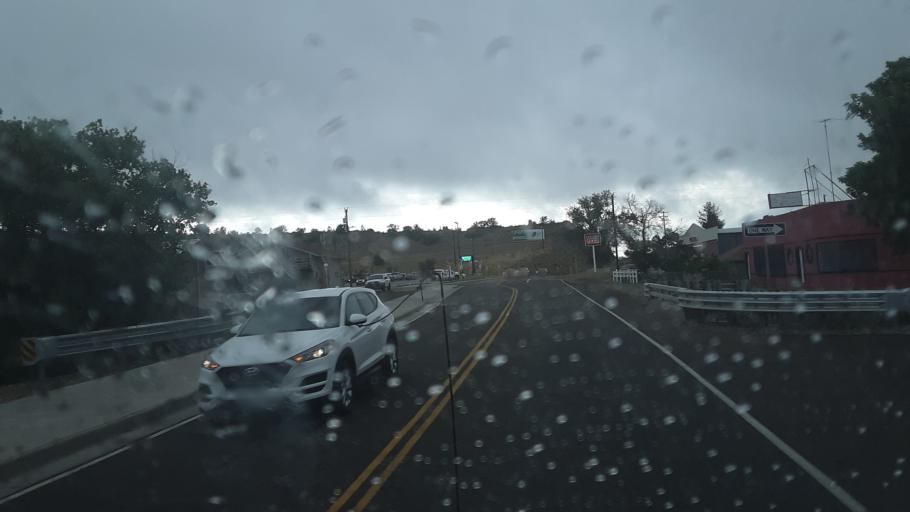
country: US
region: Colorado
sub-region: Huerfano County
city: Walsenburg
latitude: 37.6335
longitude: -104.7882
